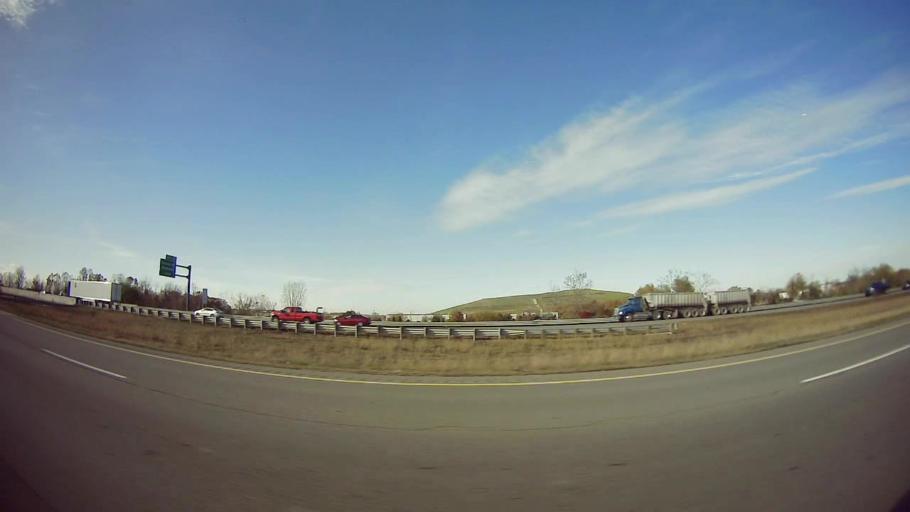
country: US
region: Michigan
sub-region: Wayne County
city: Wayne
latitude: 42.2695
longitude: -83.4407
